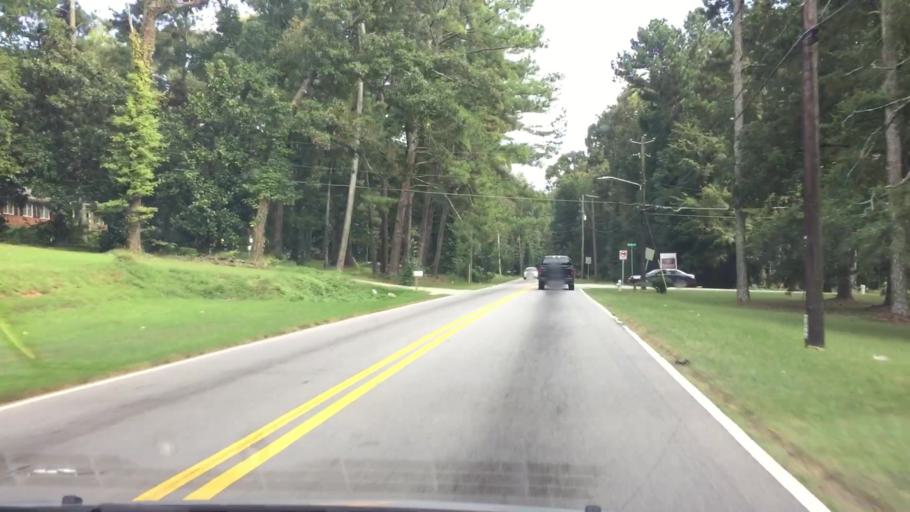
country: US
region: Georgia
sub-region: Clayton County
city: Conley
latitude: 33.6701
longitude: -84.3079
